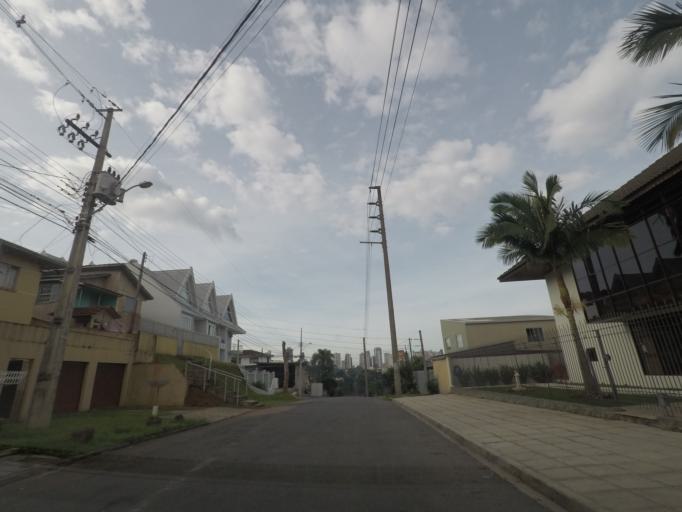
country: BR
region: Parana
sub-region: Curitiba
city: Curitiba
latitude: -25.4204
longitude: -49.2992
